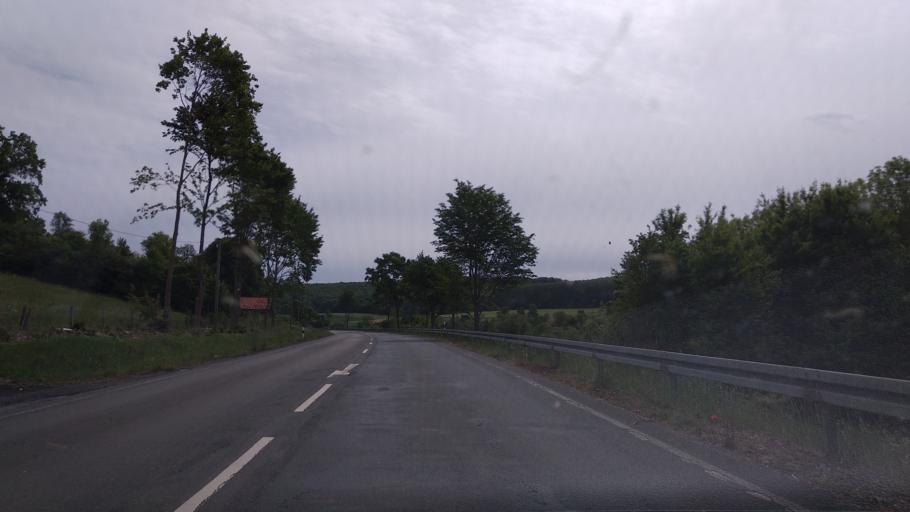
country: DE
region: North Rhine-Westphalia
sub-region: Regierungsbezirk Detmold
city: Willebadessen
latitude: 51.6270
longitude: 9.0481
